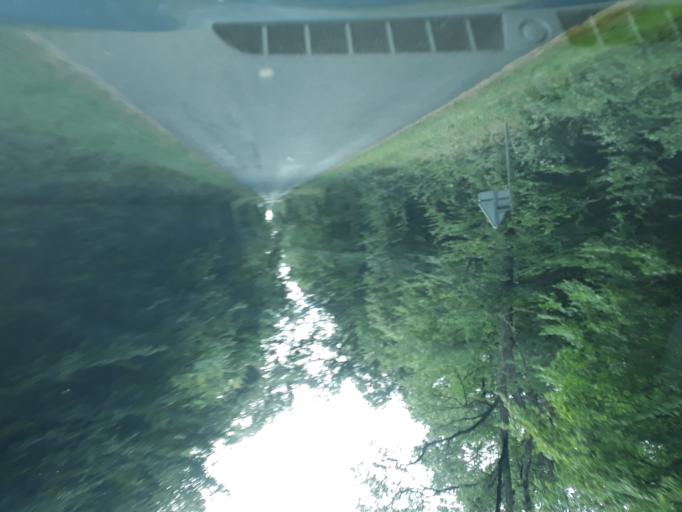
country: FR
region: Centre
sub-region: Departement du Loir-et-Cher
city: Oucques
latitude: 47.8592
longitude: 1.3969
